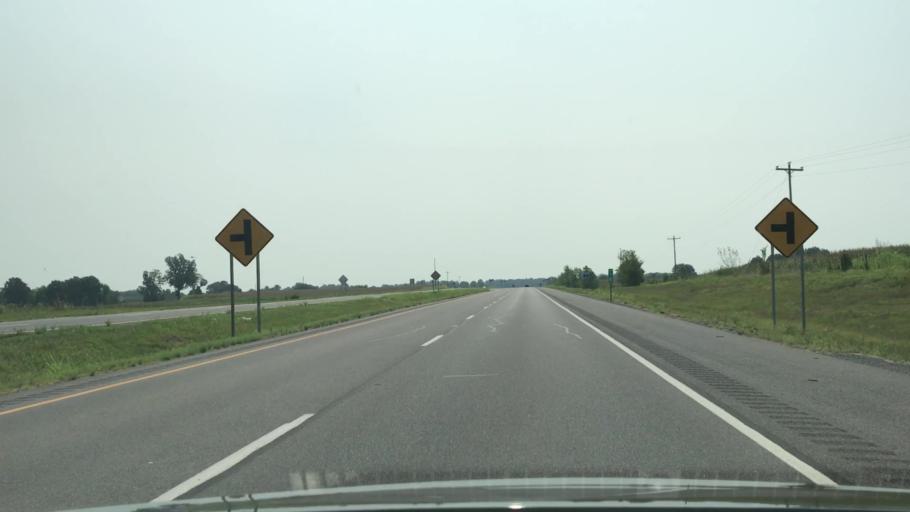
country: US
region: Kentucky
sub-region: Graves County
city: Mayfield
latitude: 36.6853
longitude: -88.5411
